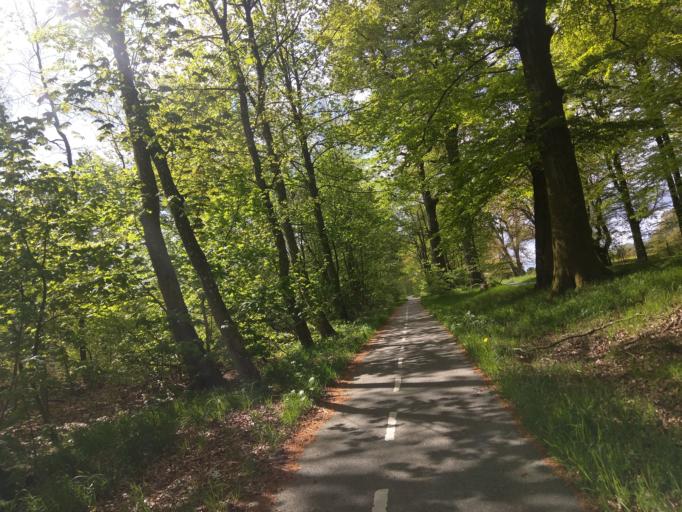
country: DK
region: Central Jutland
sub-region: Silkeborg Kommune
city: Kjellerup
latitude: 56.3236
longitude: 9.4196
